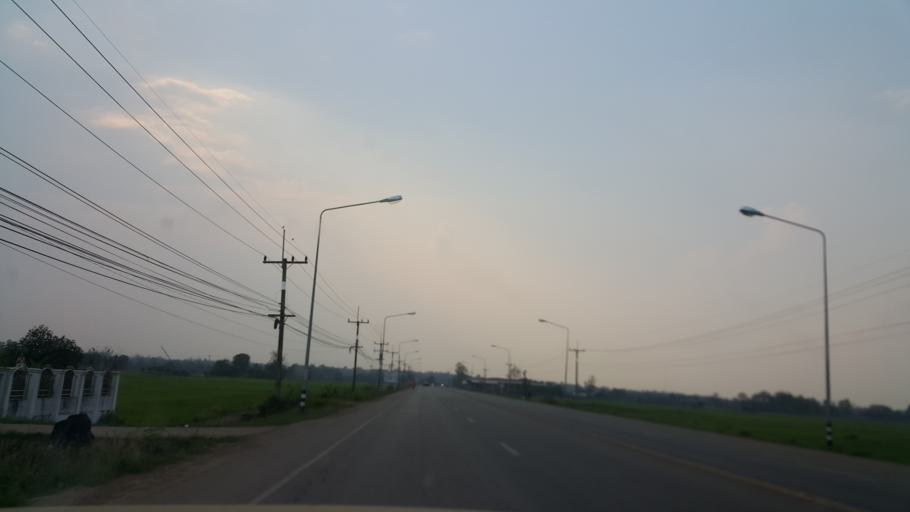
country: TH
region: Nakhon Phanom
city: Renu Nakhon
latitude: 17.0194
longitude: 104.7251
